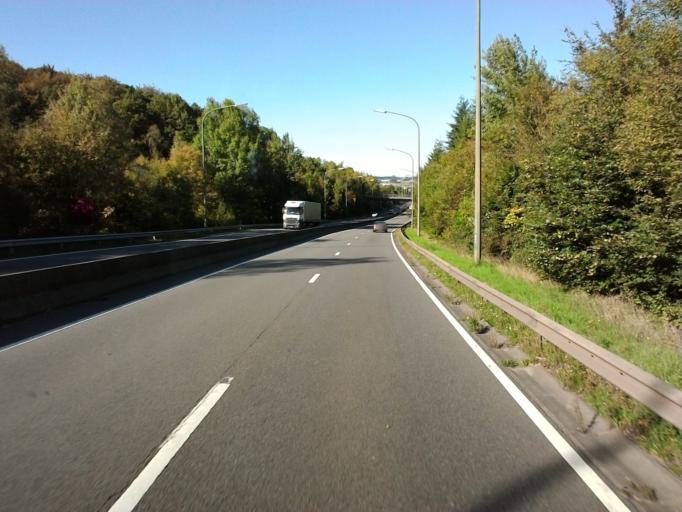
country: BE
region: Wallonia
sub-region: Province du Luxembourg
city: Messancy
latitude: 49.5972
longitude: 5.8077
